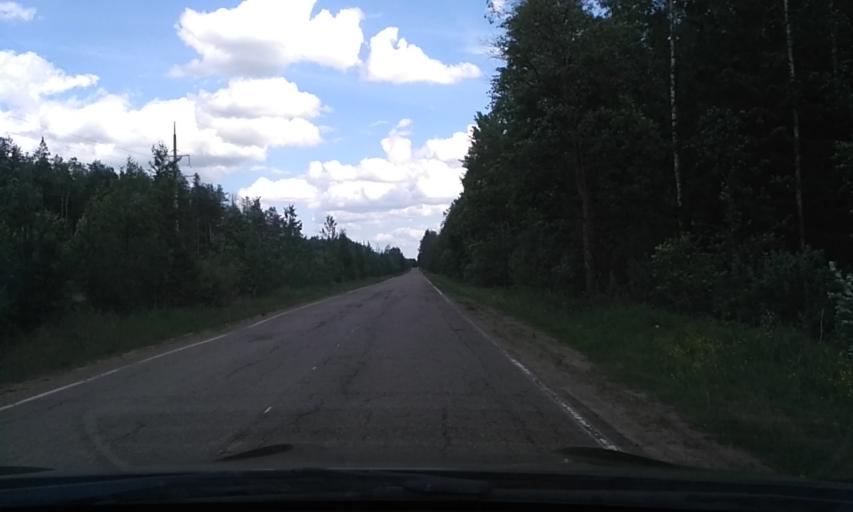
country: RU
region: Leningrad
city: Otradnoye
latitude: 59.8198
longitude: 30.8101
